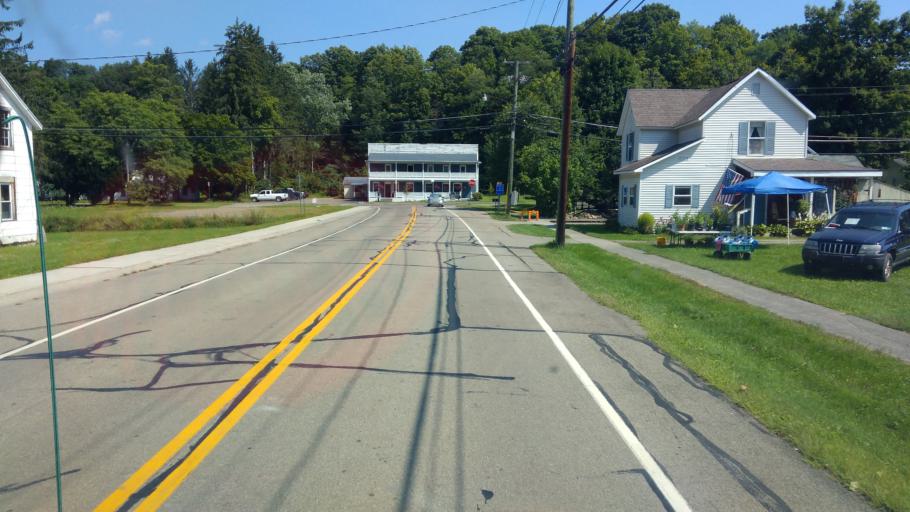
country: US
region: New York
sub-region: Allegany County
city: Belmont
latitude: 42.3071
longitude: -78.0228
